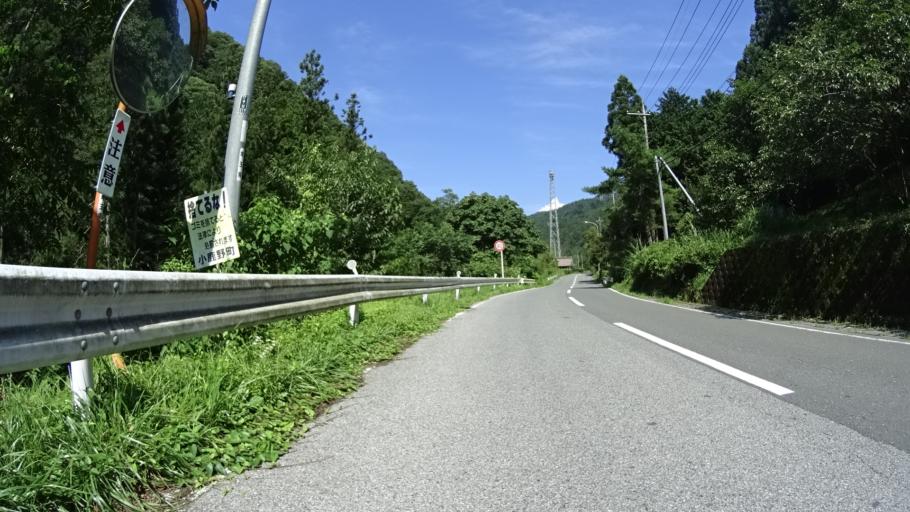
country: JP
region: Saitama
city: Chichibu
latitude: 36.0456
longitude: 138.8901
